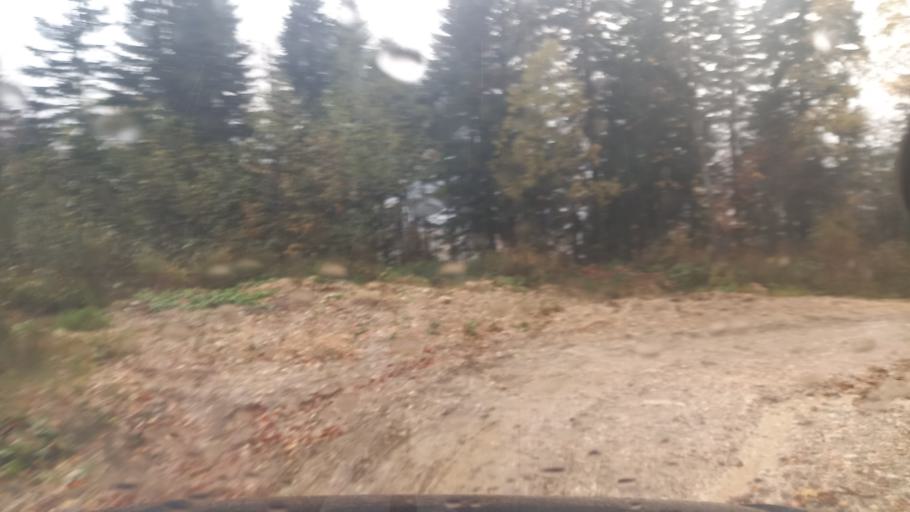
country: RU
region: Krasnodarskiy
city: Gornoye Loo
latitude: 44.0100
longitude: 39.8406
